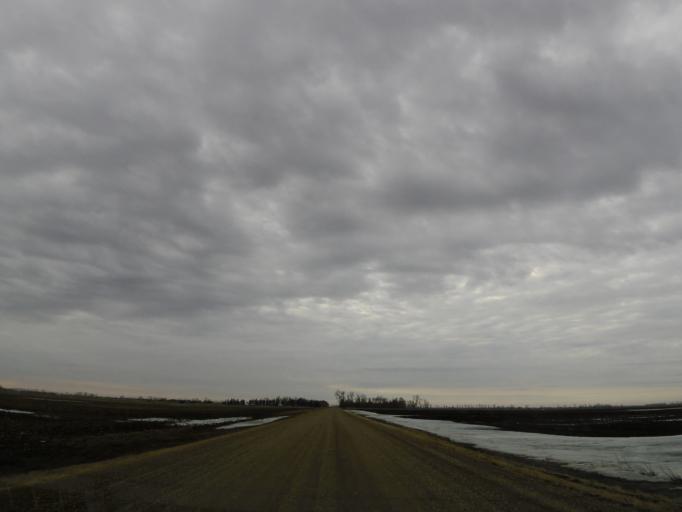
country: US
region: North Dakota
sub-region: Walsh County
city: Grafton
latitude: 48.3875
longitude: -97.4486
